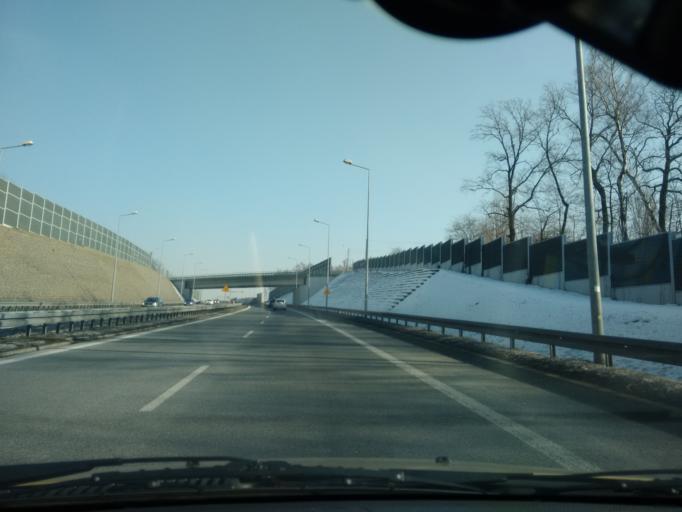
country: PL
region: Silesian Voivodeship
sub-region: Bielsko-Biala
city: Bielsko-Biala
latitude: 49.8431
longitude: 19.0804
